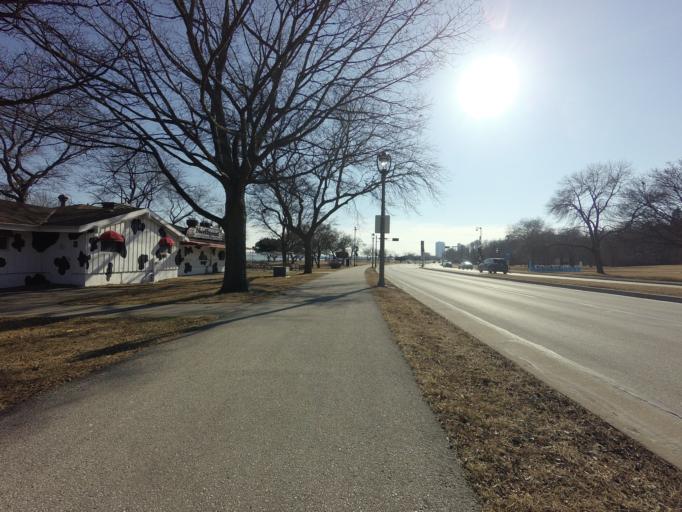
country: US
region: Wisconsin
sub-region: Milwaukee County
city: Shorewood
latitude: 43.0583
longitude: -87.8767
